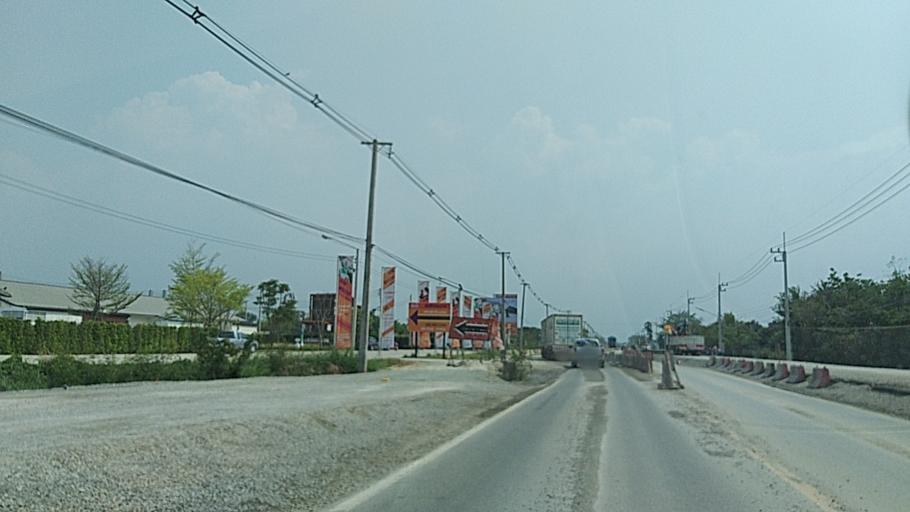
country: TH
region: Chon Buri
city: Phanat Nikhom
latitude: 13.4199
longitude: 101.1869
